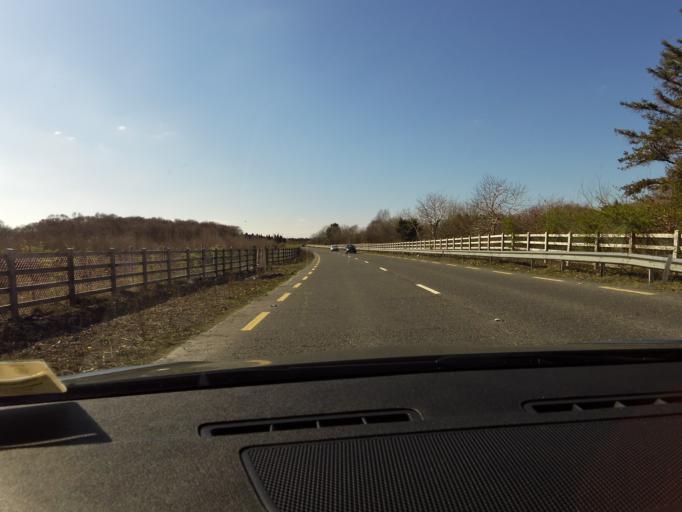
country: IE
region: Connaught
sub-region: County Galway
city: Oughterard
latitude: 53.3984
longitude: -9.2629
